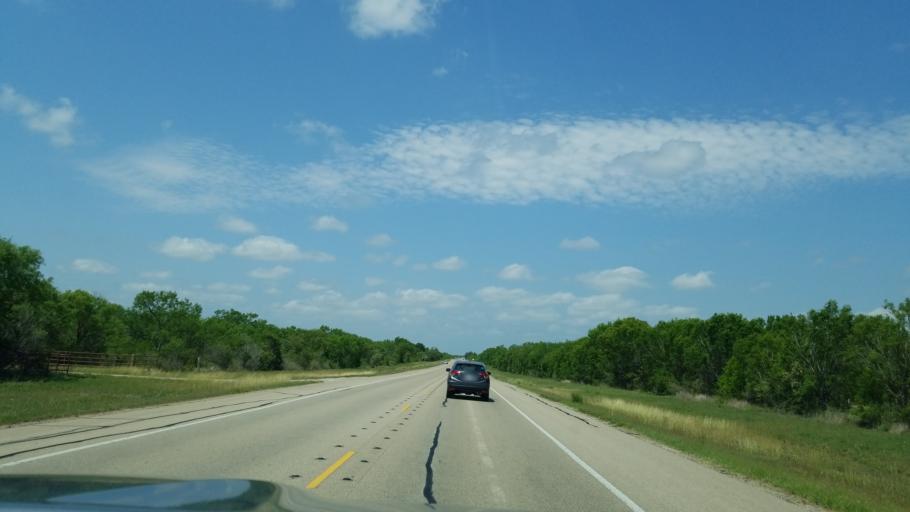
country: US
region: Texas
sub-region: Frio County
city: Pearsall
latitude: 29.0106
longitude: -99.1313
